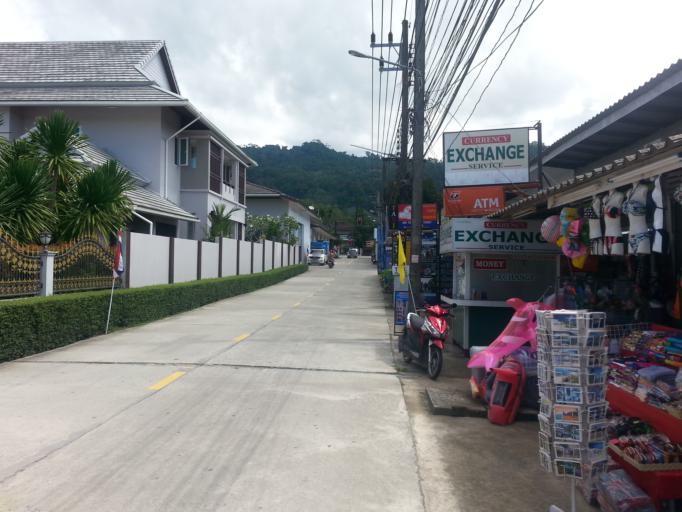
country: TH
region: Phangnga
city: Ban Khao Lak
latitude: 8.6451
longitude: 98.2505
